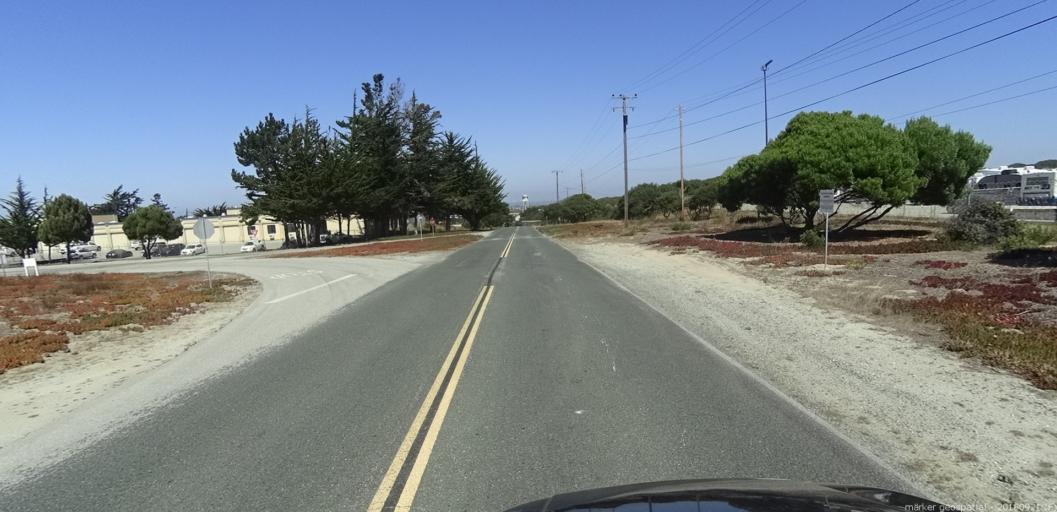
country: US
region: California
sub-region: Monterey County
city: Marina
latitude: 36.6479
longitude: -121.7871
